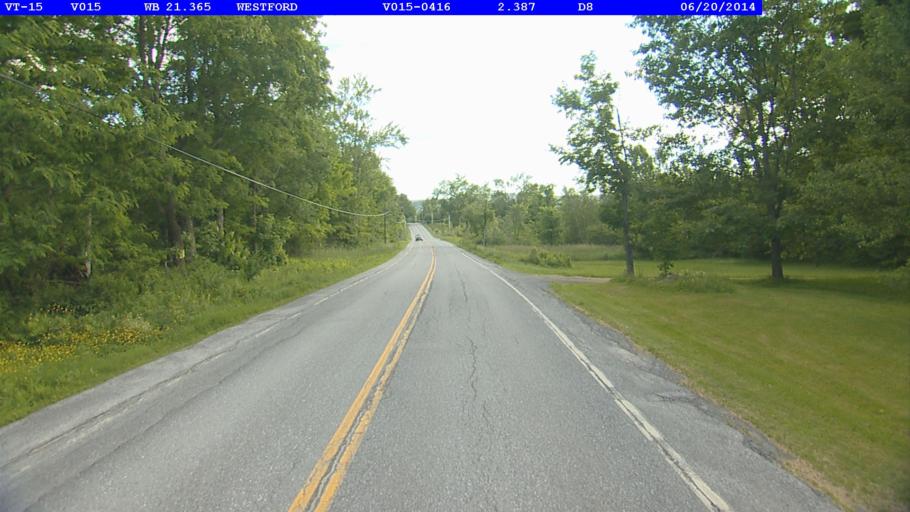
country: US
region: Vermont
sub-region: Chittenden County
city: Jericho
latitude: 44.6265
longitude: -72.9211
